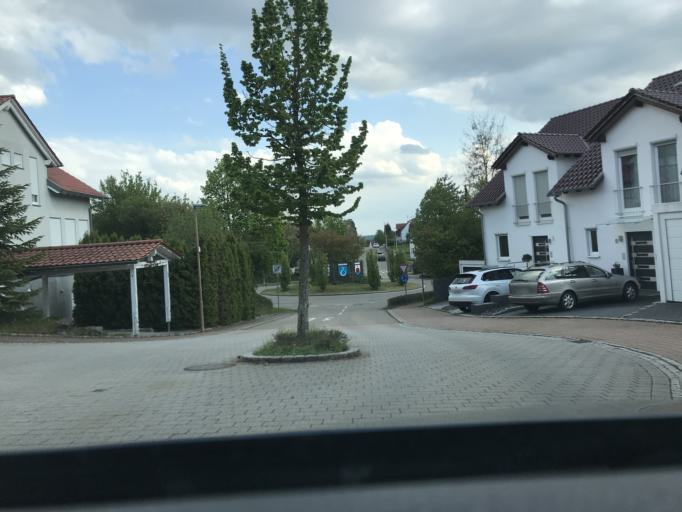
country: DE
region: Baden-Wuerttemberg
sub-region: Regierungsbezirk Stuttgart
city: Brackenheim
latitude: 49.0810
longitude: 9.0758
